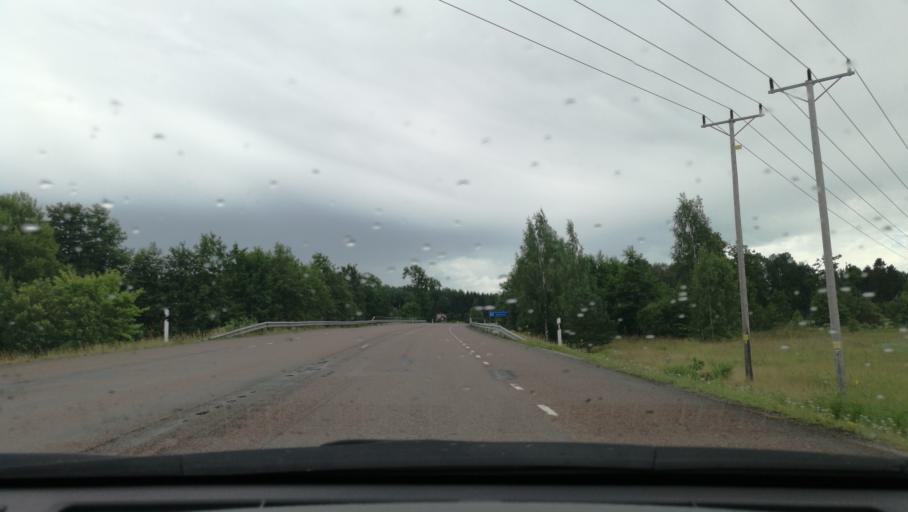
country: SE
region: Vaestmanland
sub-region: Kopings Kommun
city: Koping
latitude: 59.4781
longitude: 15.9892
